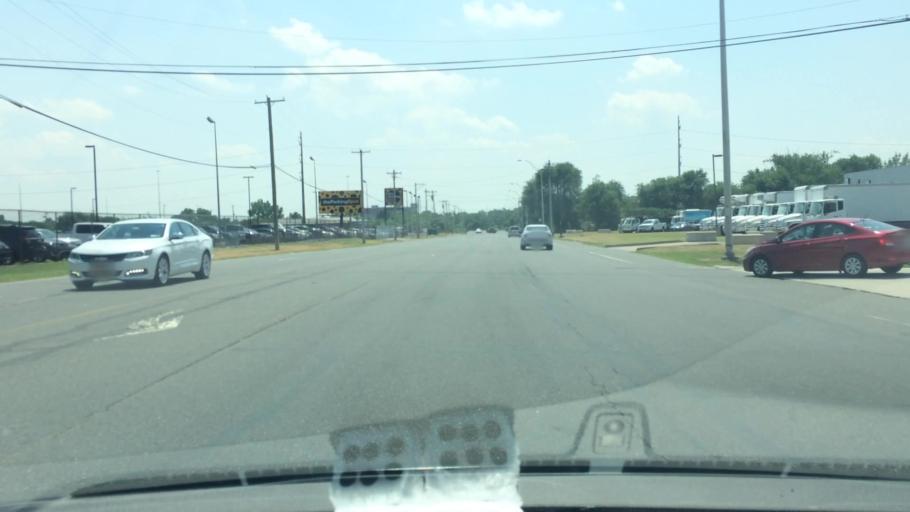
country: US
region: Pennsylvania
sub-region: Delaware County
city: Colwyn
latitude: 39.8981
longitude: -75.2263
